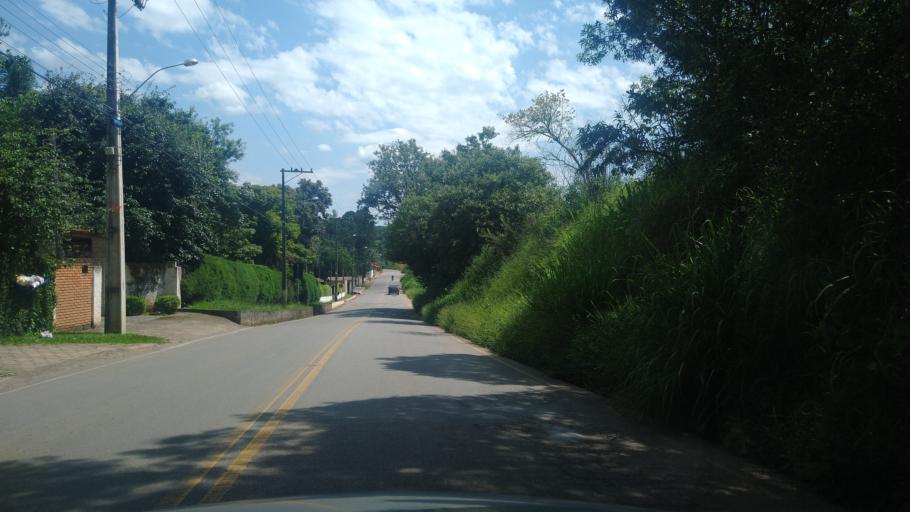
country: BR
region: Minas Gerais
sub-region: Extrema
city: Extrema
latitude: -22.8137
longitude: -46.3017
